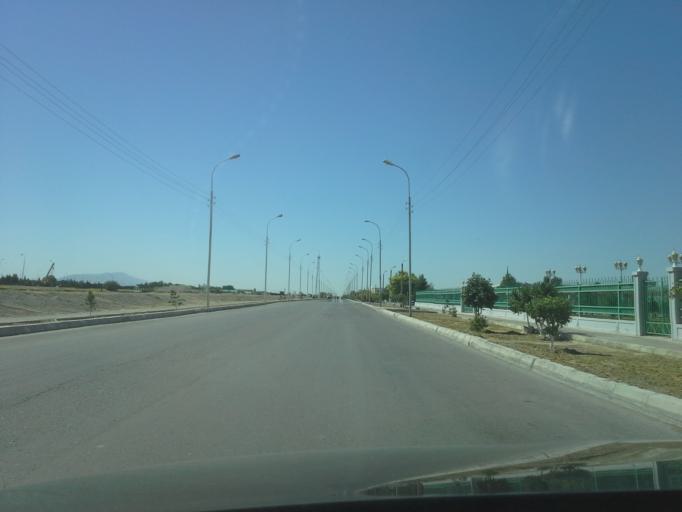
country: TM
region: Ahal
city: Abadan
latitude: 38.0481
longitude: 58.1983
